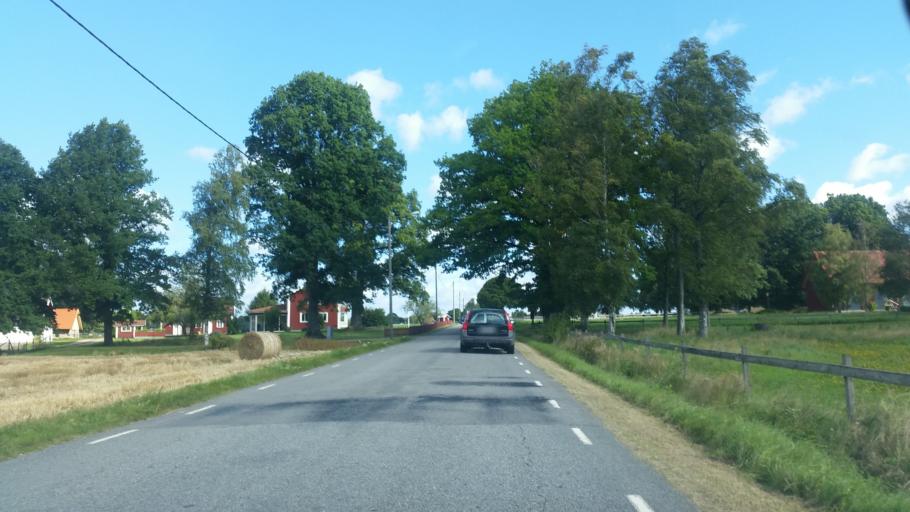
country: SE
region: Joenkoeping
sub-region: Varnamo Kommun
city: Forsheda
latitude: 57.1770
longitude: 13.8432
